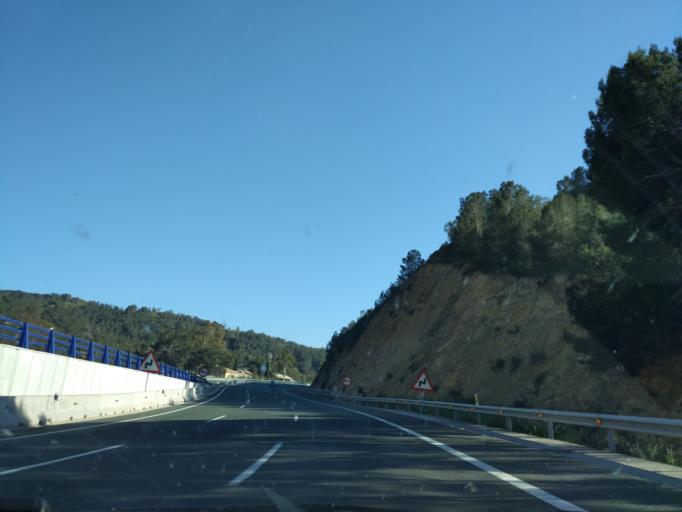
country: ES
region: Murcia
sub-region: Murcia
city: Murcia
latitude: 37.9008
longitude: -1.1433
